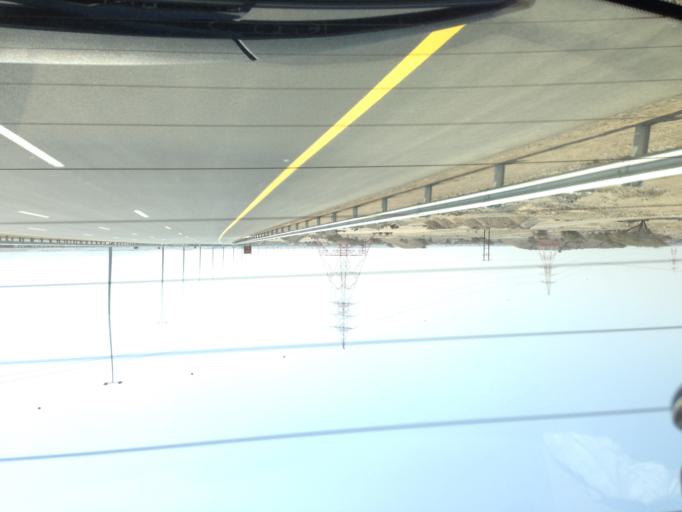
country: OM
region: Al Batinah
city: Rustaq
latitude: 23.5379
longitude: 57.5275
